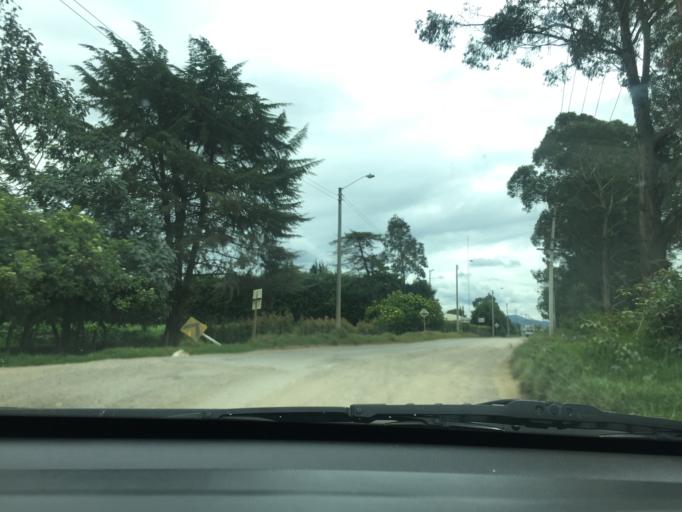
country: CO
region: Cundinamarca
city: El Rosal
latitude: 4.8129
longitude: -74.2610
